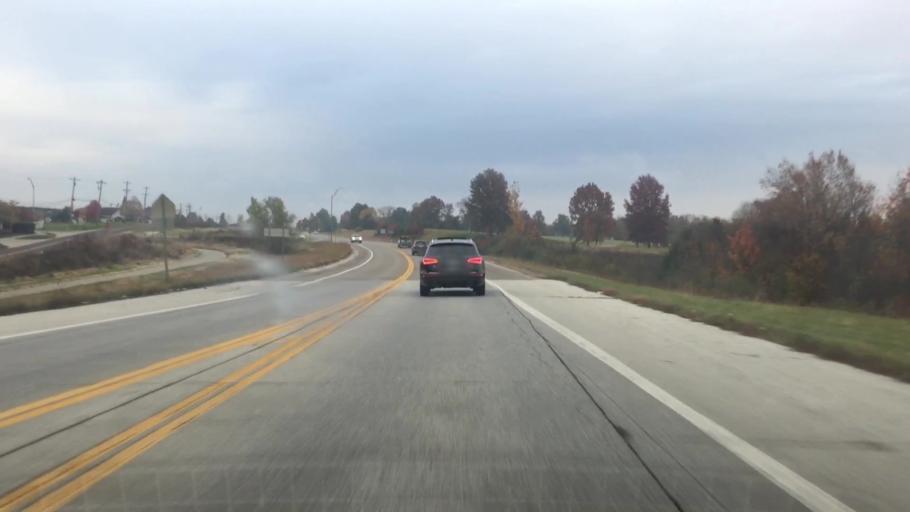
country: US
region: Missouri
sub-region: Boone County
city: Columbia
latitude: 38.8938
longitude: -92.3355
